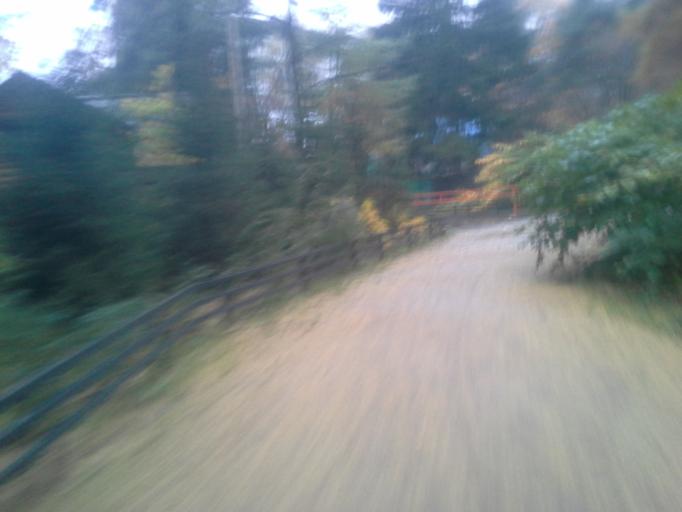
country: RU
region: Moscow
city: Solntsevo
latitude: 55.6606
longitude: 37.3695
